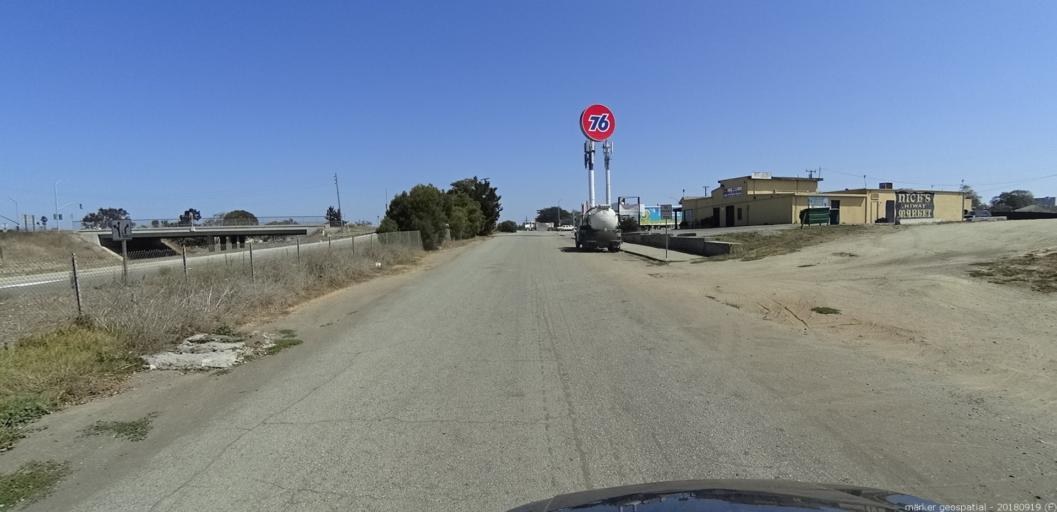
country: US
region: California
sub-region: Monterey County
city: Castroville
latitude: 36.7603
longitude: -121.7531
